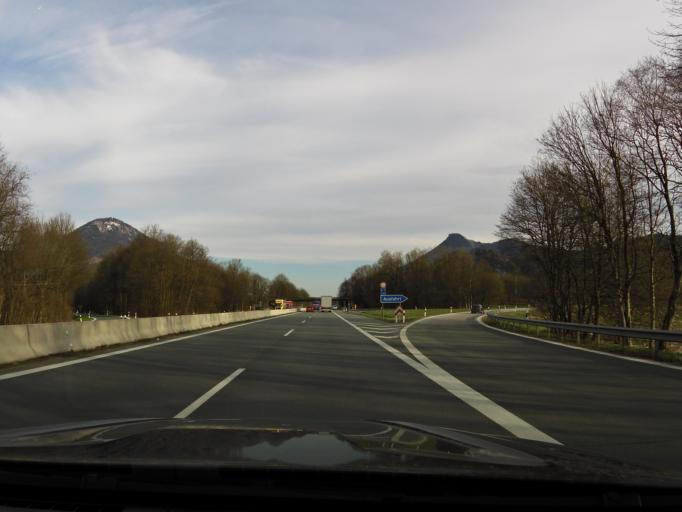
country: DE
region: Bavaria
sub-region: Upper Bavaria
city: Oberaudorf
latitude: 47.6444
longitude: 12.1909
